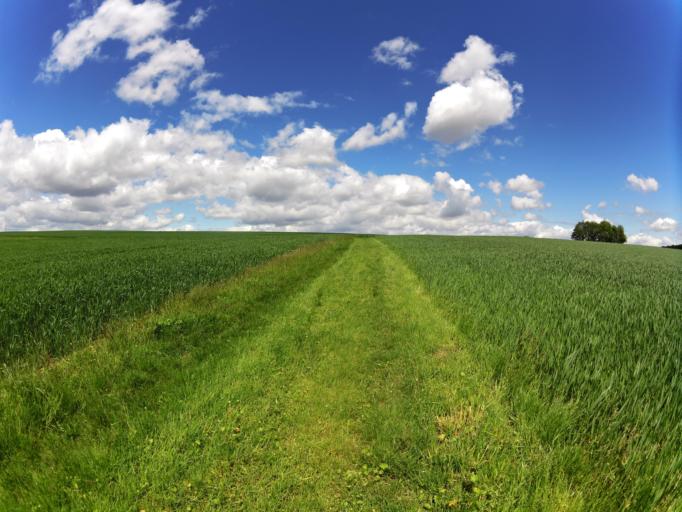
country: DE
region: Bavaria
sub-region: Regierungsbezirk Unterfranken
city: Volkach
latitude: 49.8756
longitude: 10.2454
